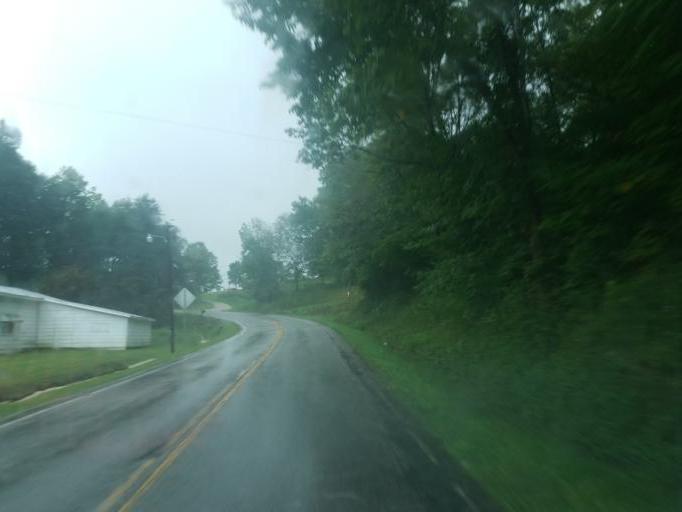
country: US
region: Kentucky
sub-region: Rowan County
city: Morehead
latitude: 38.2711
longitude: -83.3237
